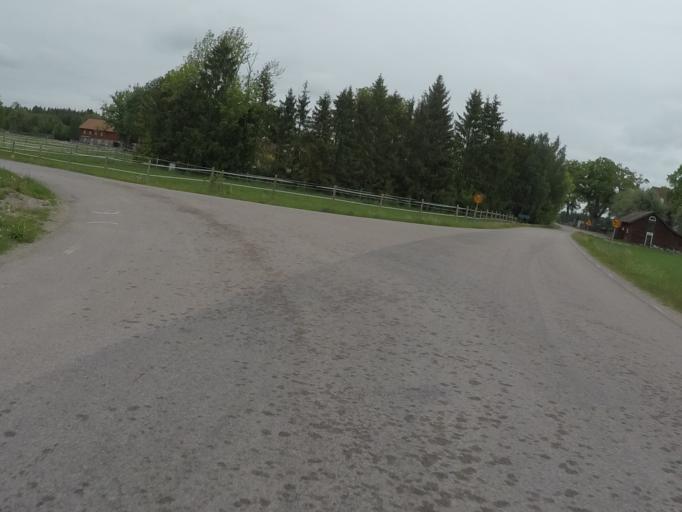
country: SE
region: Vaestmanland
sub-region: Hallstahammars Kommun
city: Kolback
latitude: 59.5471
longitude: 16.3105
